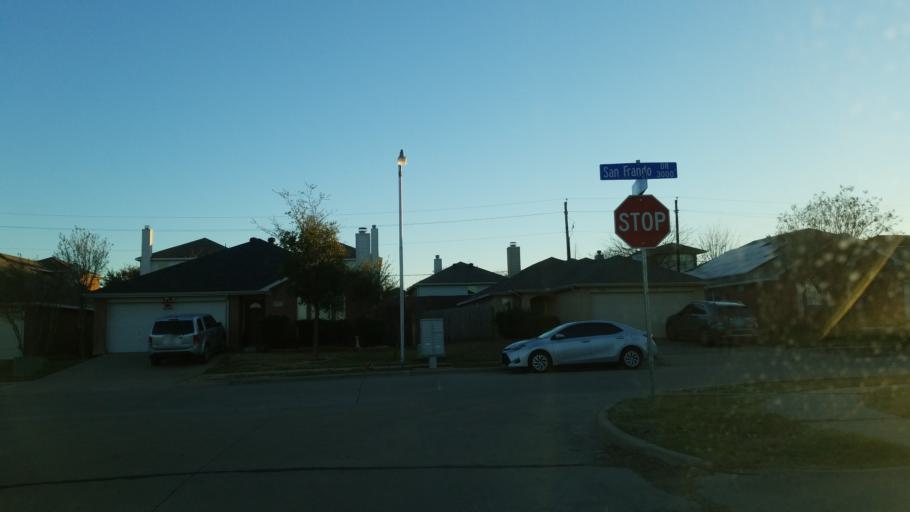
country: US
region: Texas
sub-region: Tarrant County
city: Arlington
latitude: 32.7238
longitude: -97.0549
